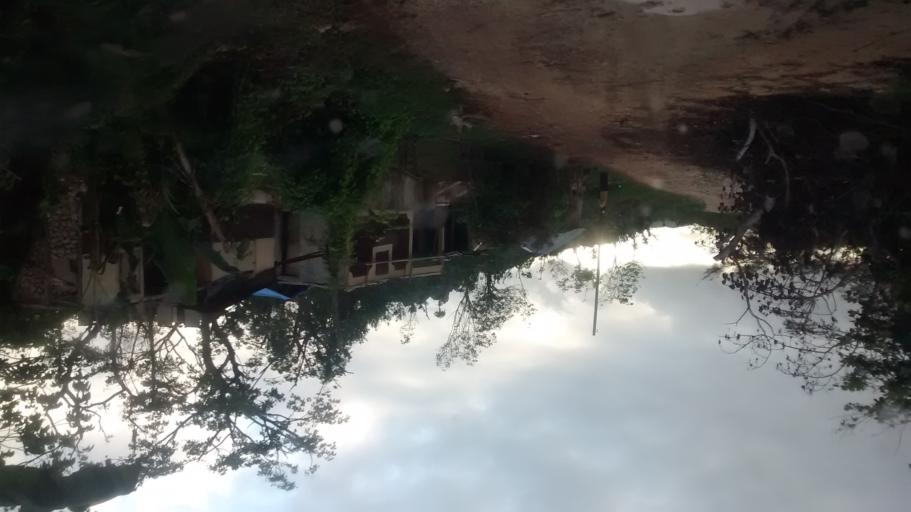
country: HT
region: Grandans
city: Corail
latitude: 18.4761
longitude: -73.7957
